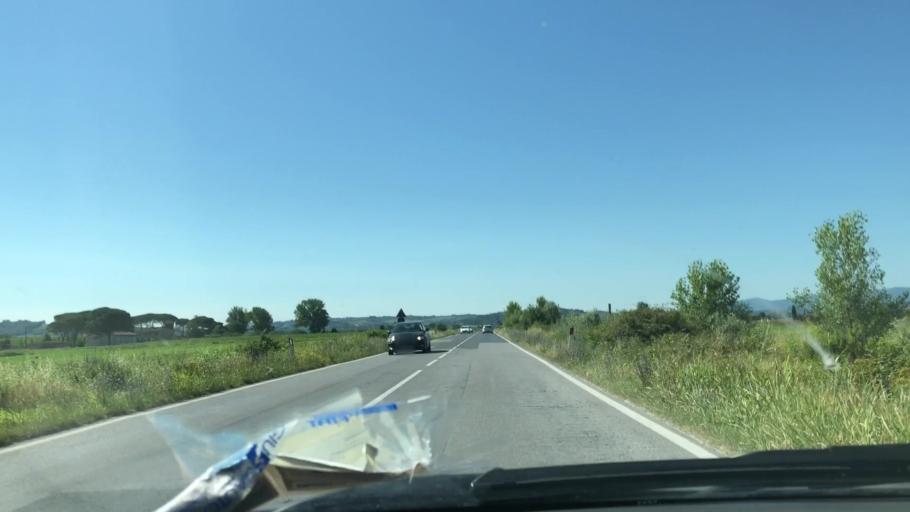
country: IT
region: Tuscany
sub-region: Province of Pisa
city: Forcoli
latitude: 43.5937
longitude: 10.6991
